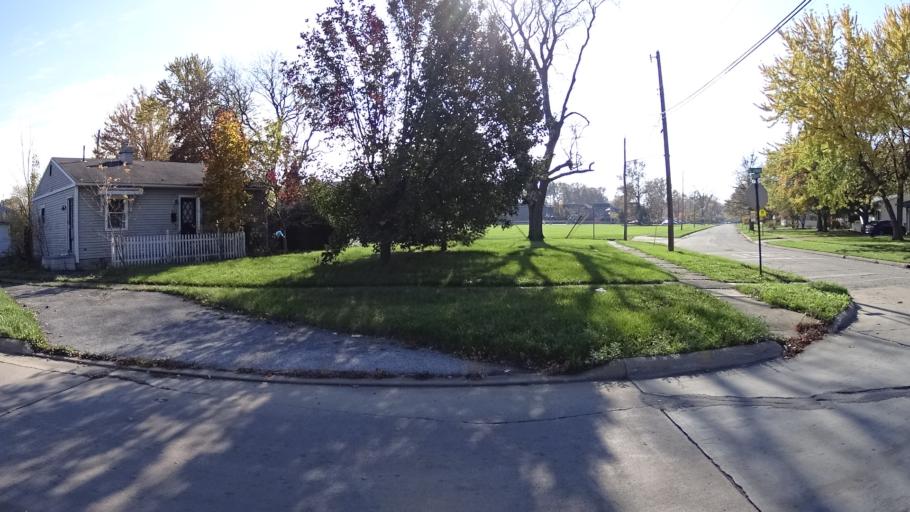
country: US
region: Ohio
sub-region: Lorain County
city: Lorain
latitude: 41.4747
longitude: -82.1439
